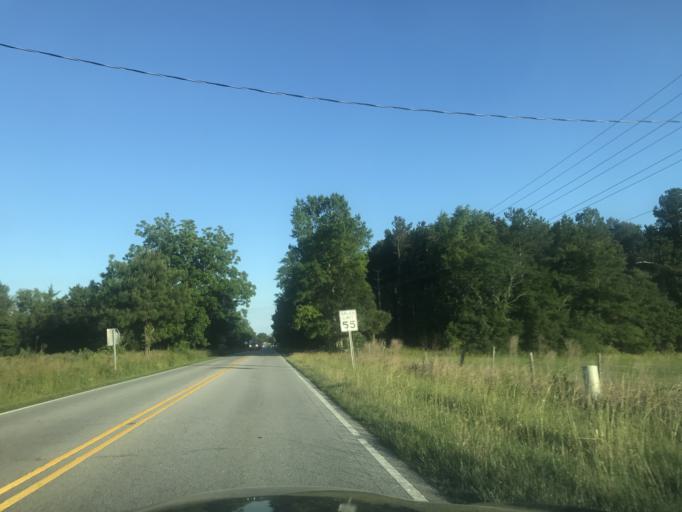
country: US
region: North Carolina
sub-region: Johnston County
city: Archer Lodge
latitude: 35.6899
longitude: -78.3709
